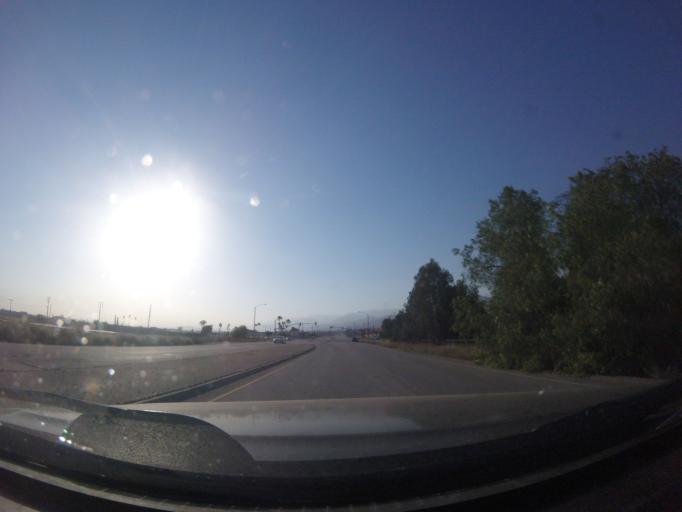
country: US
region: California
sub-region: San Bernardino County
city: Highland
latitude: 34.1071
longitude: -117.1840
